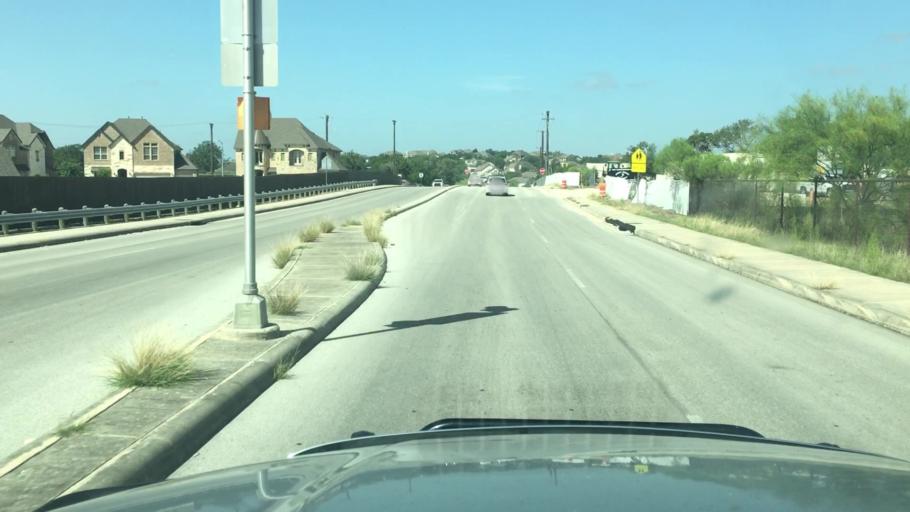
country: US
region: Texas
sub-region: Bexar County
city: Timberwood Park
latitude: 29.6700
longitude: -98.4563
